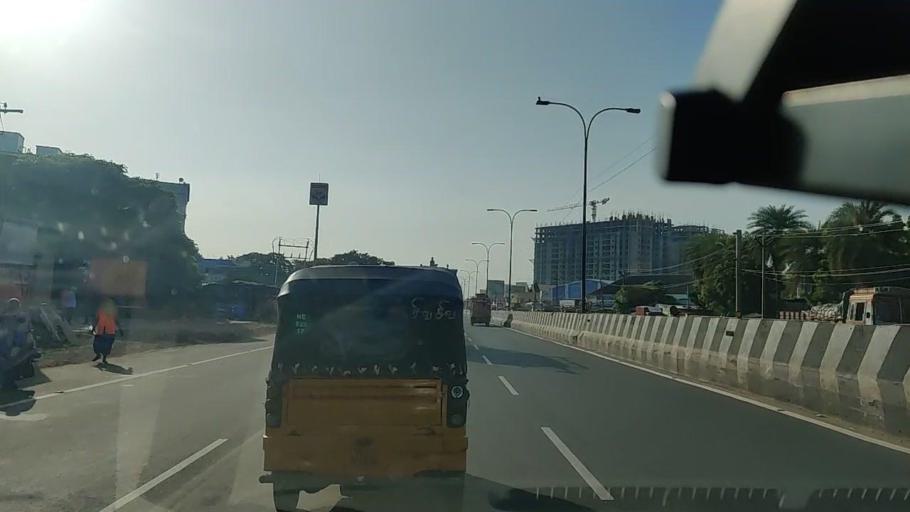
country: IN
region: Tamil Nadu
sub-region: Thiruvallur
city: Chinnasekkadu
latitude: 13.1438
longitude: 80.2212
